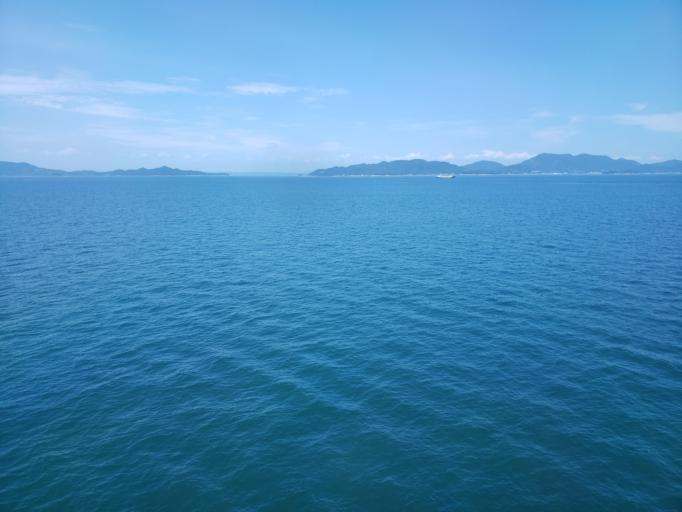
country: JP
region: Kagawa
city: Tonosho
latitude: 34.4057
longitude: 134.1506
